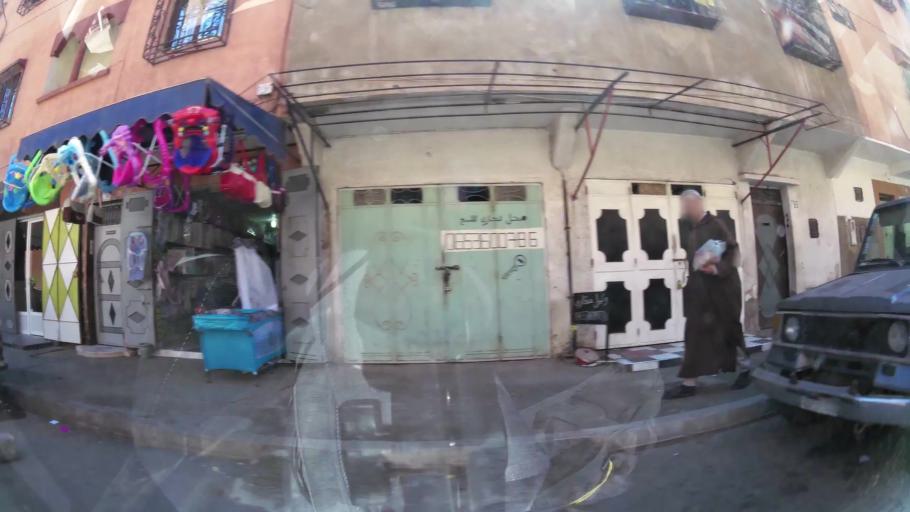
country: MA
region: Marrakech-Tensift-Al Haouz
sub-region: Marrakech
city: Marrakesh
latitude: 31.6298
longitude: -8.0594
